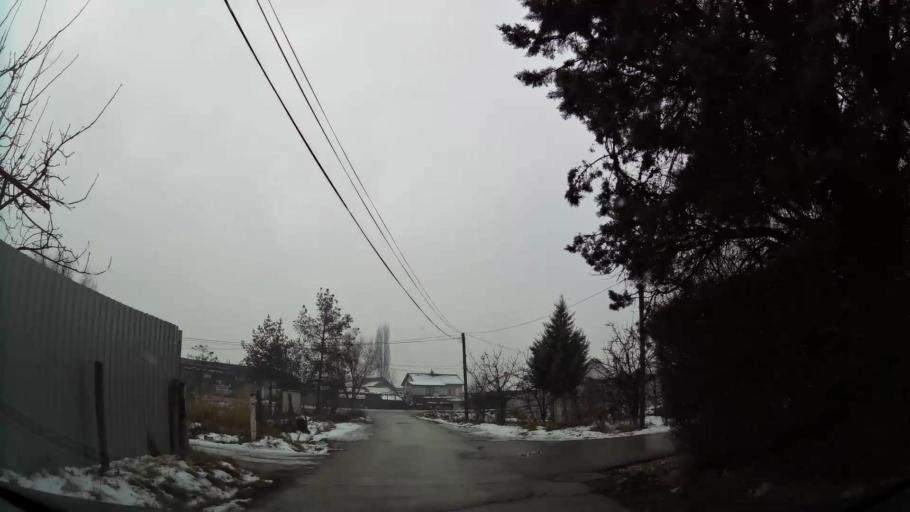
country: MK
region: Petrovec
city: Petrovec
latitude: 41.9399
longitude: 21.6145
